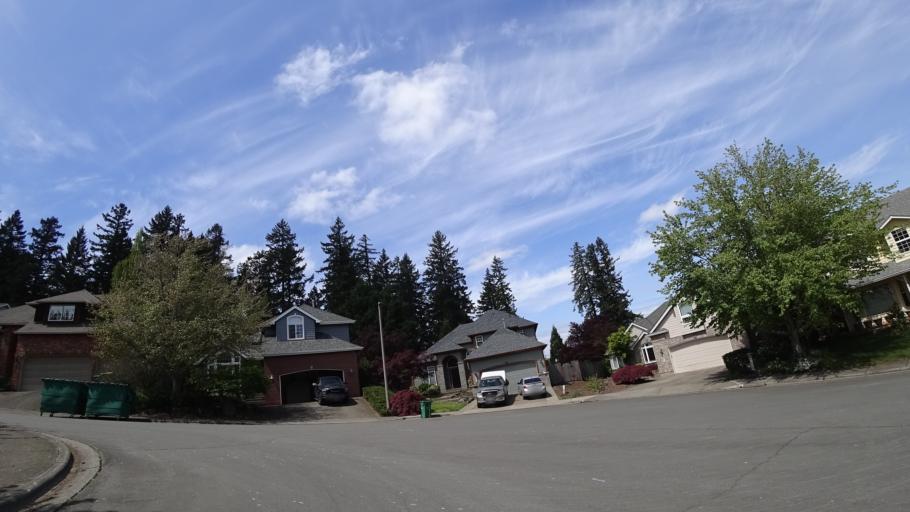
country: US
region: Oregon
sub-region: Washington County
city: Aloha
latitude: 45.4656
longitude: -122.8913
